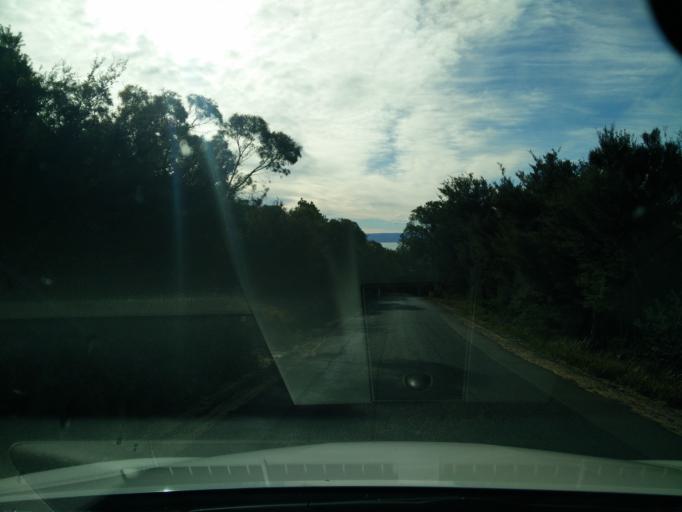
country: AU
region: Tasmania
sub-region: Break O'Day
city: St Helens
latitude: -42.1377
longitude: 148.3020
